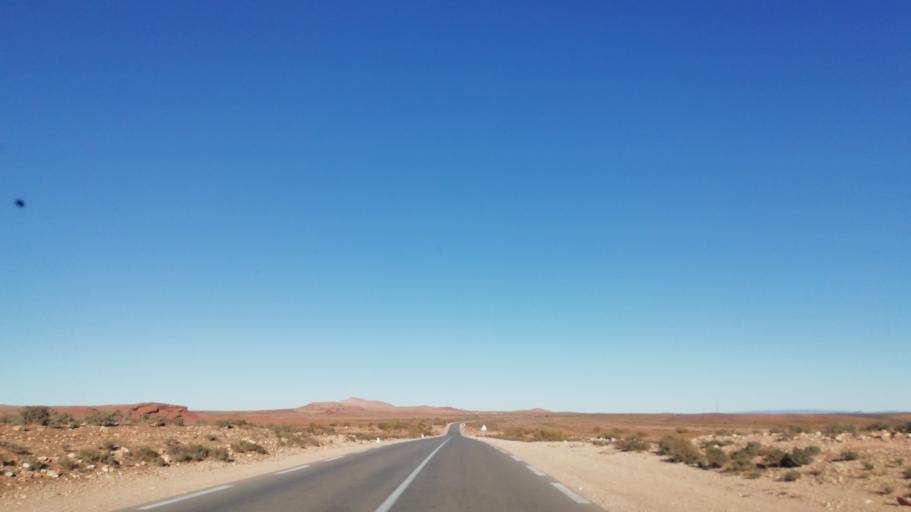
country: DZ
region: El Bayadh
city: El Abiodh Sidi Cheikh
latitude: 33.1060
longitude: 0.2168
